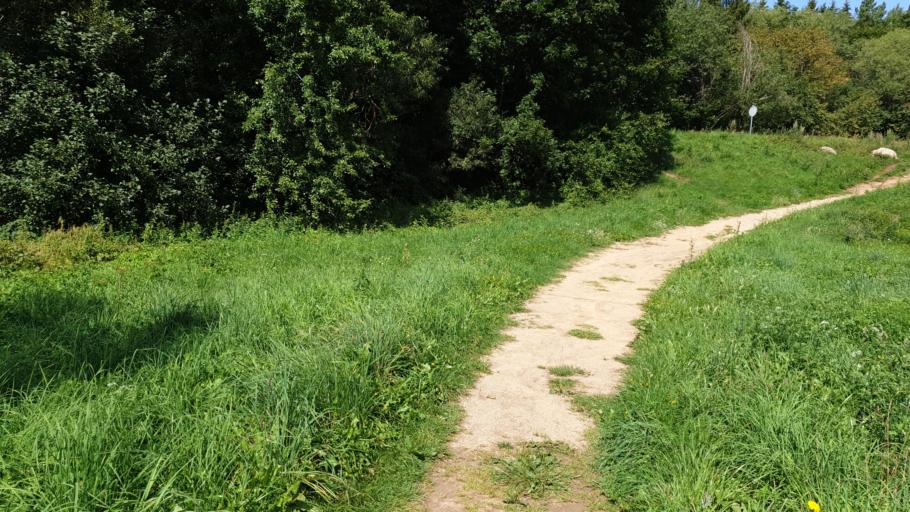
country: LT
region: Vilnius County
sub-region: Vilniaus Rajonas
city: Vievis
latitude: 54.8264
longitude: 24.9459
